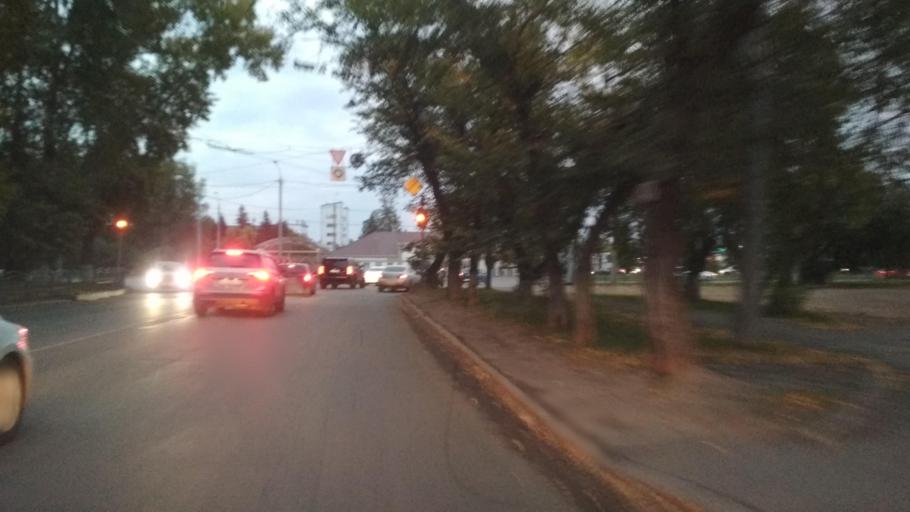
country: RU
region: Tomsk
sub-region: Tomskiy Rayon
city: Tomsk
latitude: 56.4761
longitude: 85.0147
